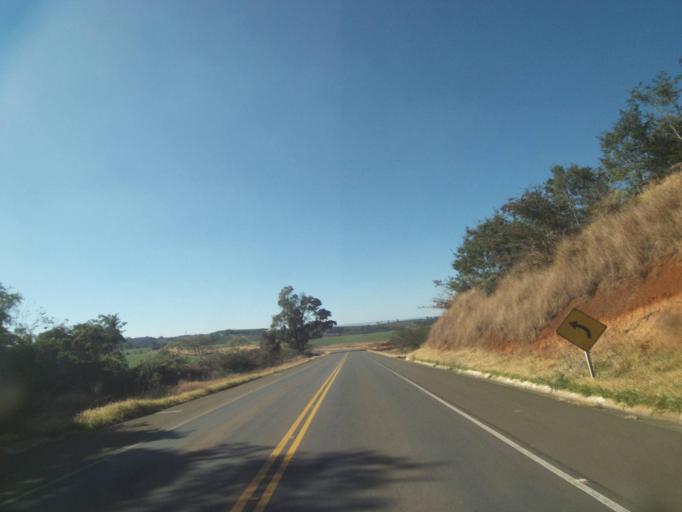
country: BR
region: Parana
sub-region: Tibagi
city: Tibagi
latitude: -24.7485
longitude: -50.4636
